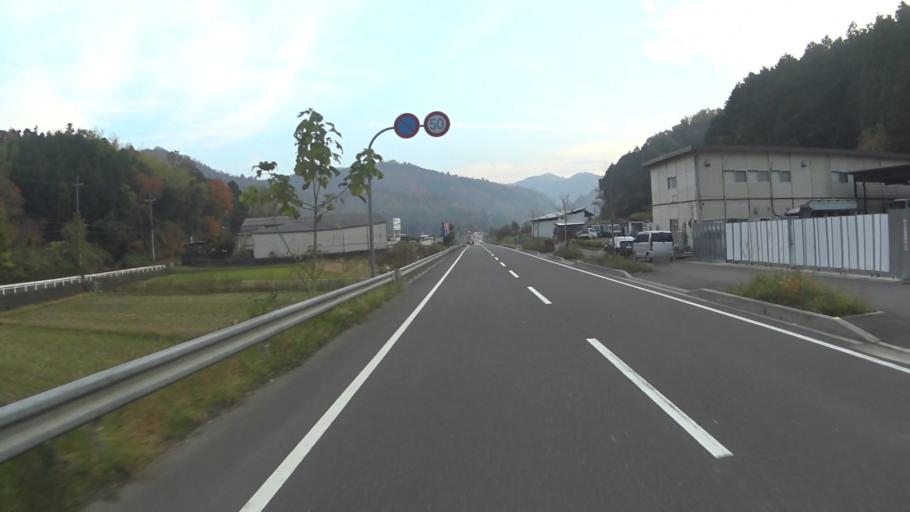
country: JP
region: Kyoto
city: Maizuru
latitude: 35.4677
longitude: 135.4235
